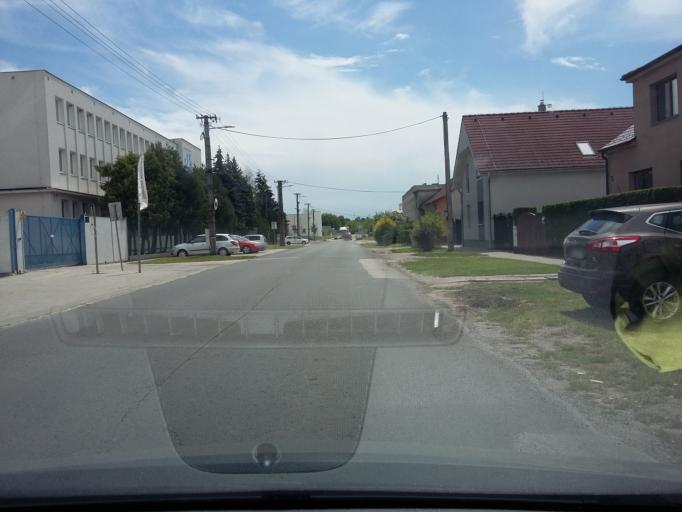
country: SK
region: Bratislavsky
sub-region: Okres Malacky
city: Malacky
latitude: 48.4328
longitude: 17.0267
